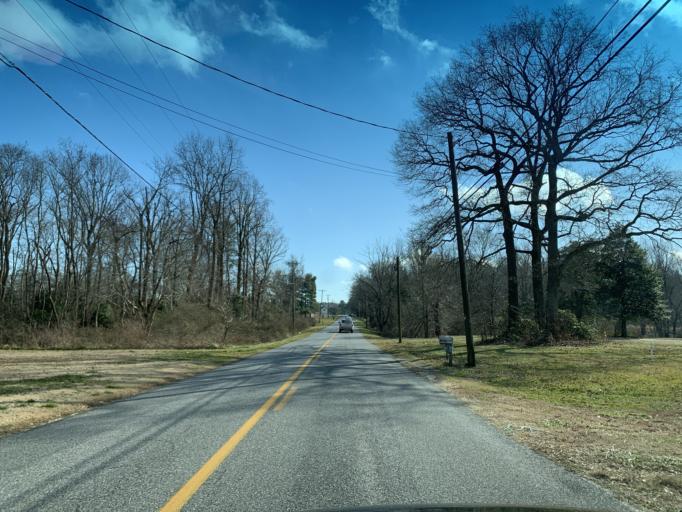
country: US
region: Delaware
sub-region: Sussex County
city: Selbyville
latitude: 38.4397
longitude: -75.1899
